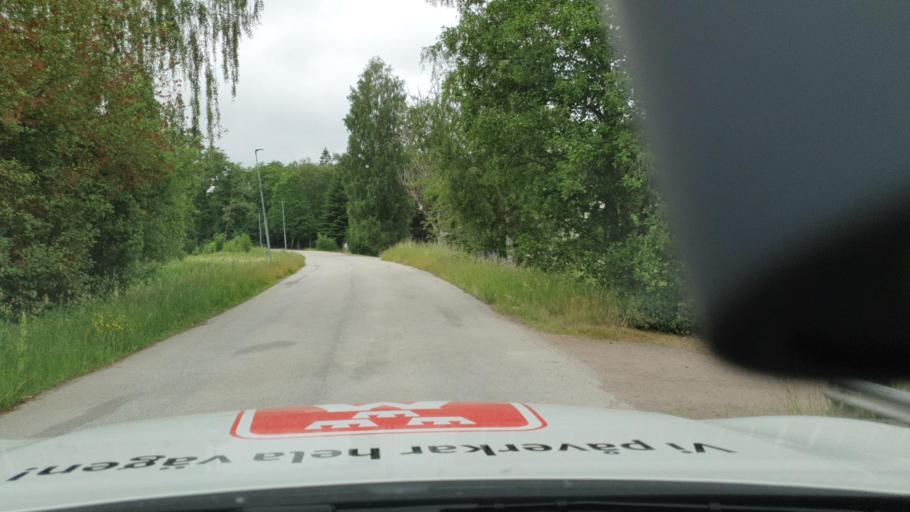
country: SE
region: Vaestra Goetaland
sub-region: Tibro Kommun
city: Tibro
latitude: 58.4050
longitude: 14.1370
